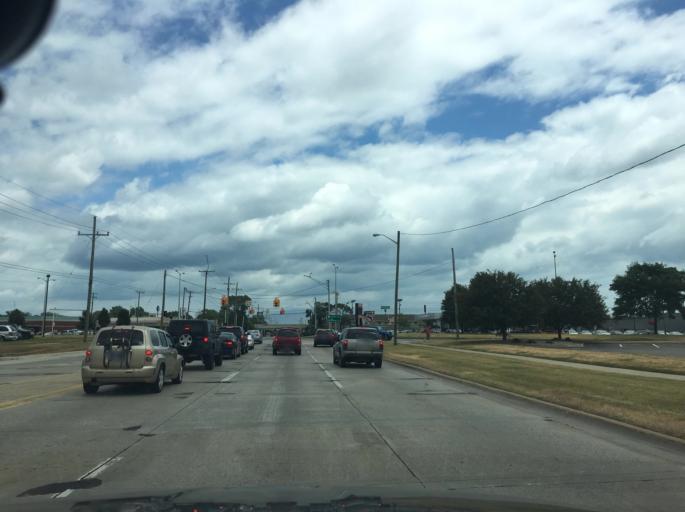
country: US
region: Michigan
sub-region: Macomb County
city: Roseville
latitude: 42.5246
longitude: -82.9202
